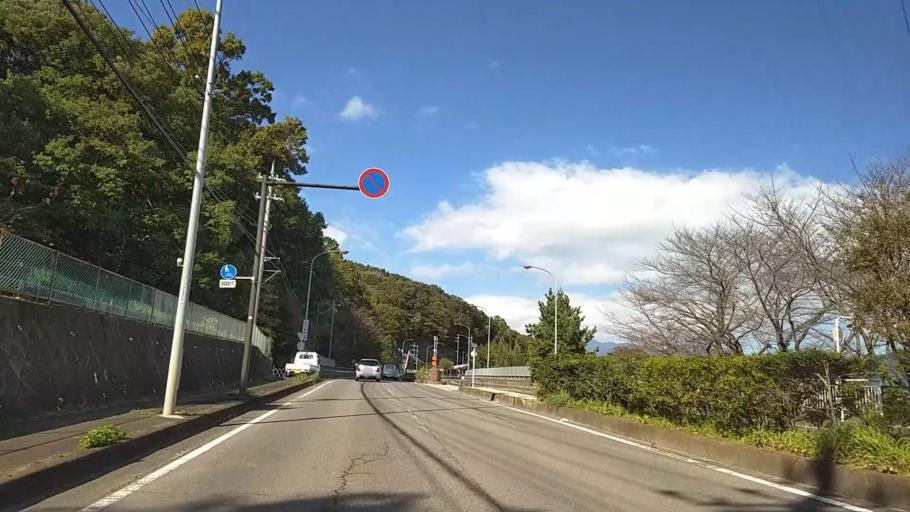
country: JP
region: Kanagawa
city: Ninomiya
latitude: 35.3271
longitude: 139.2341
